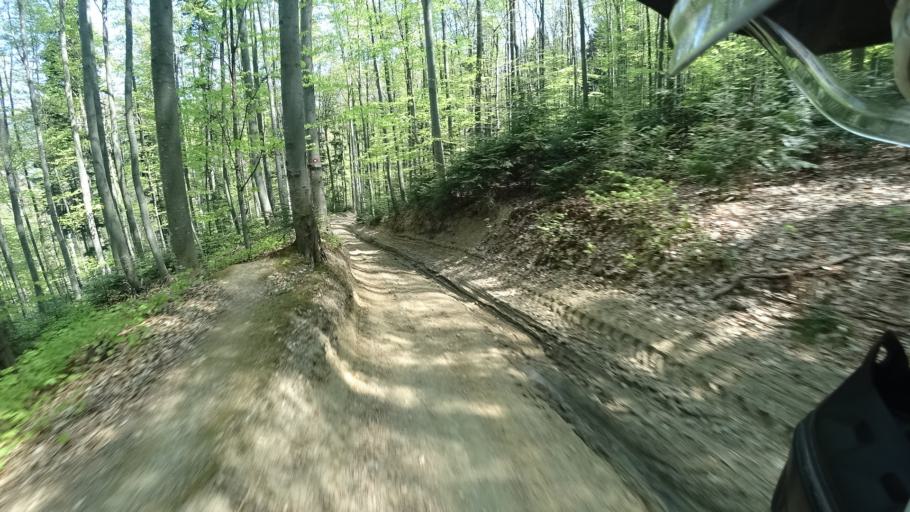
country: HR
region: Zagrebacka
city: Jablanovec
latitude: 45.9003
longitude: 15.9199
